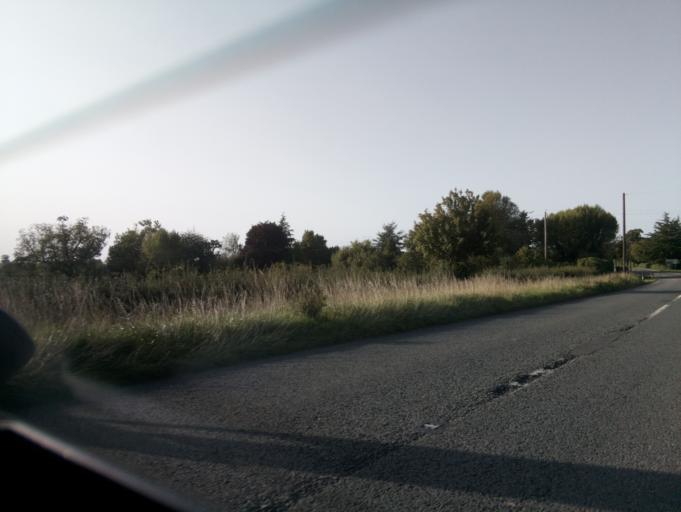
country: GB
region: England
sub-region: Gloucestershire
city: Gloucester
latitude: 51.9403
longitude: -2.2964
